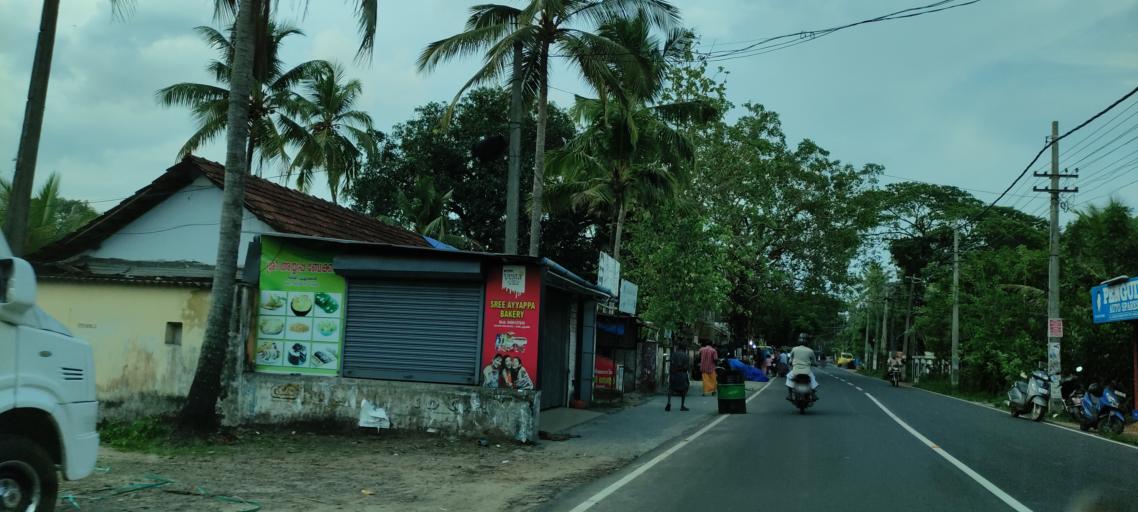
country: IN
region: Kerala
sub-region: Alappuzha
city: Kutiatodu
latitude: 9.7926
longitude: 76.3587
